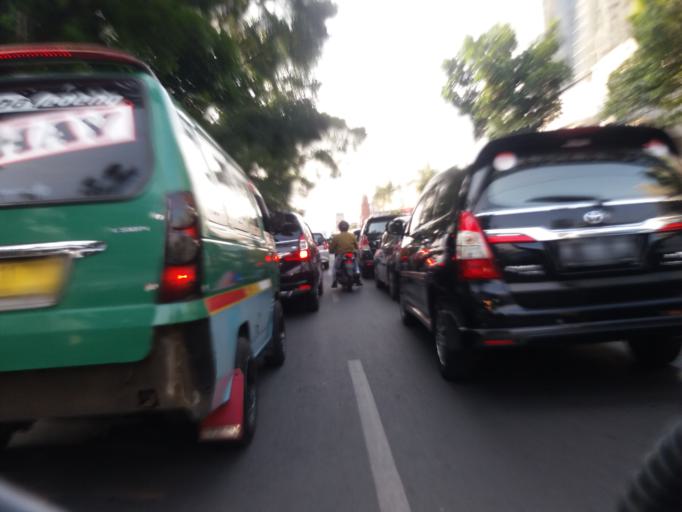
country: ID
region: West Java
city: Bandung
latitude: -6.9236
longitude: 107.6175
